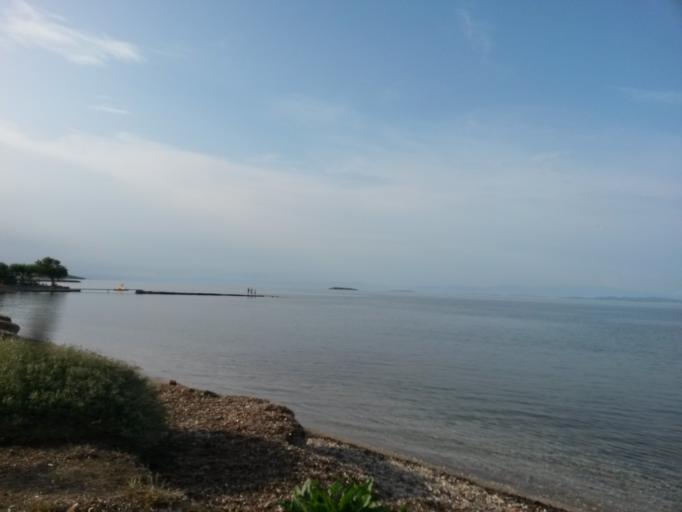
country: GR
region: North Aegean
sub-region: Nomos Lesvou
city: Pamfylla
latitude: 39.1783
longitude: 26.5023
